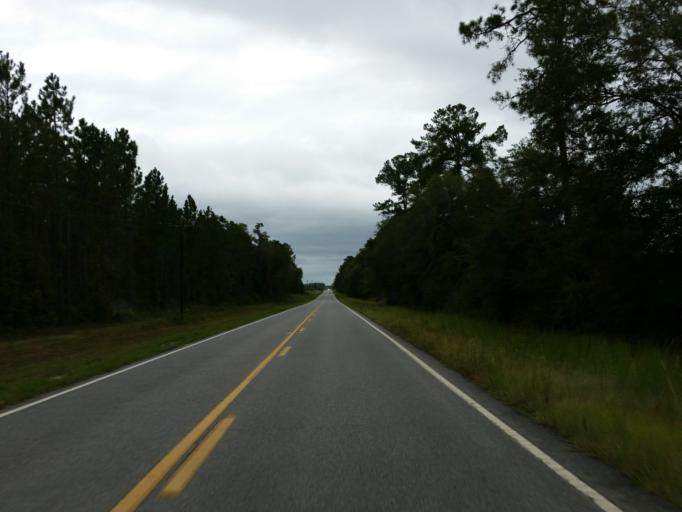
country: US
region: Georgia
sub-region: Lanier County
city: Lakeland
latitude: 30.8817
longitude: -83.0030
